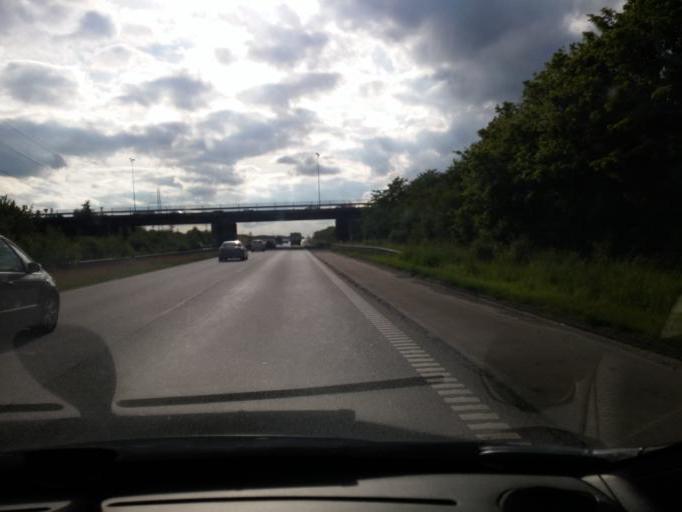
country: DK
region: Zealand
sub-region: Ringsted Kommune
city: Ringsted
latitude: 55.4555
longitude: 11.7922
